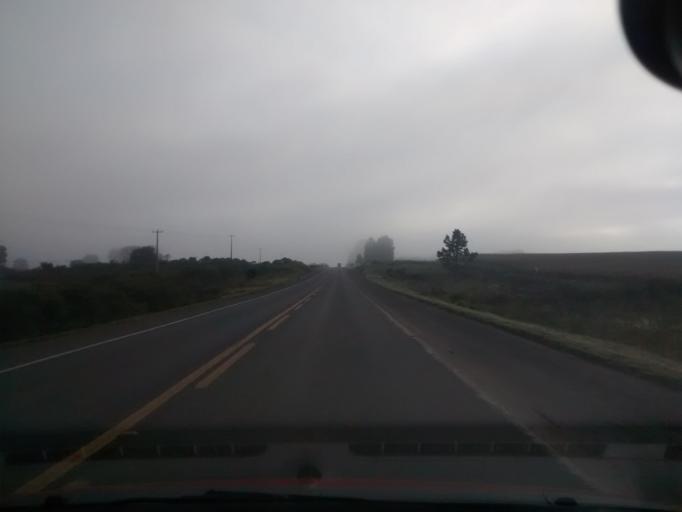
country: BR
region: Rio Grande do Sul
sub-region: Vacaria
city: Vacaria
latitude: -28.4661
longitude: -50.8913
